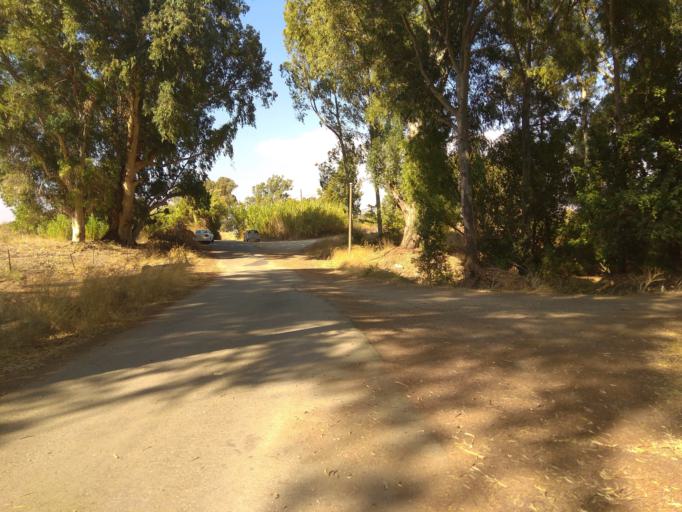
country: IL
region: Northern District
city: Qiryat Shemona
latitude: 33.2350
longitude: 35.6287
